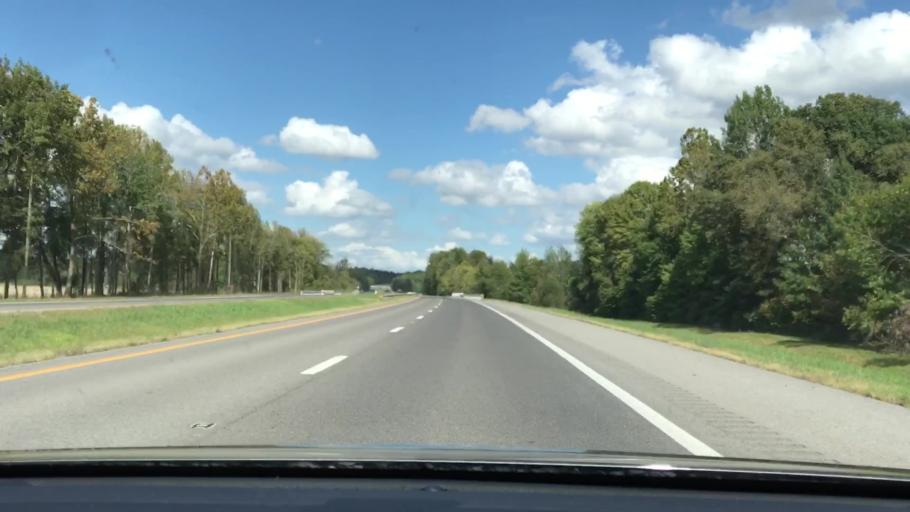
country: US
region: Kentucky
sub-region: Graves County
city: Mayfield
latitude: 36.8036
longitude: -88.4959
